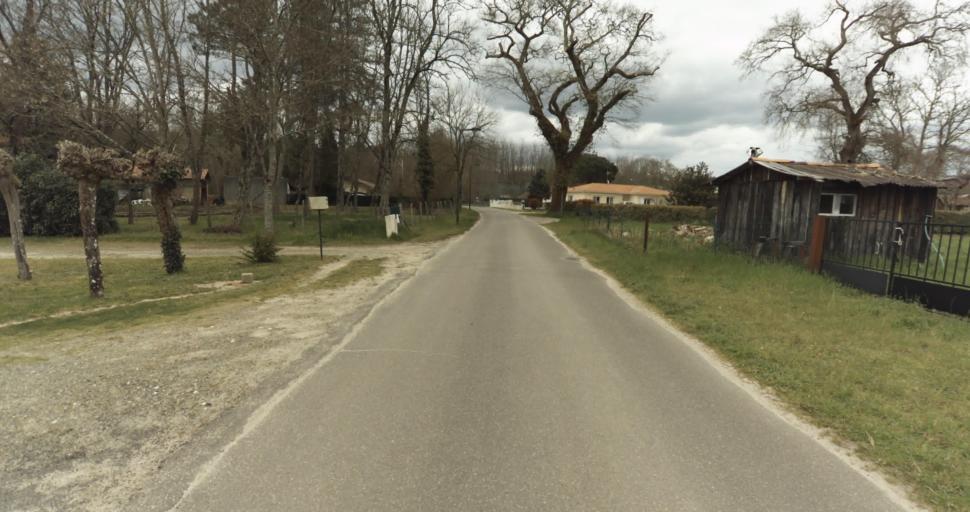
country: FR
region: Aquitaine
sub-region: Departement des Landes
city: Roquefort
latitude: 44.0361
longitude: -0.3090
